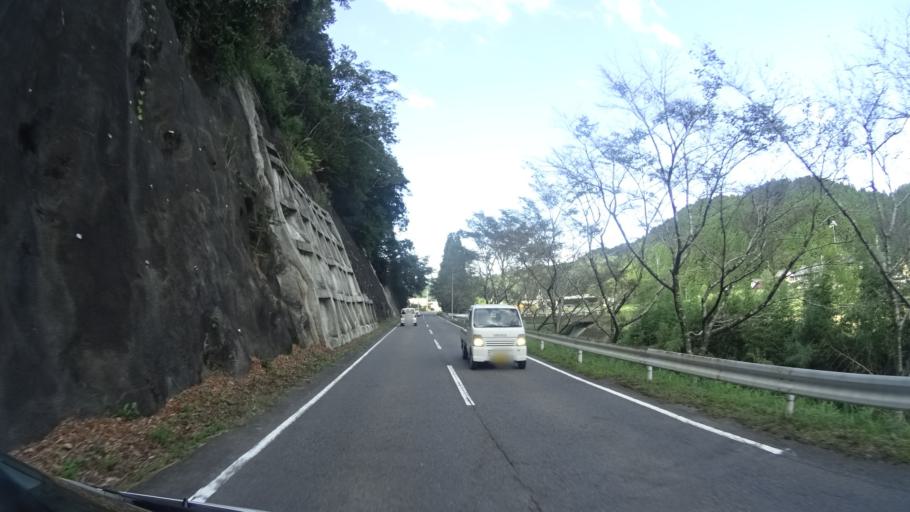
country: JP
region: Gifu
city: Minokamo
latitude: 35.5872
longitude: 137.0853
